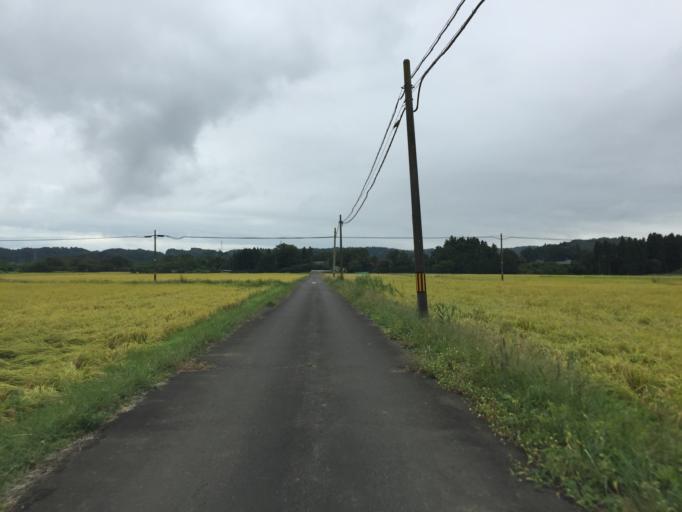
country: JP
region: Fukushima
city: Nihommatsu
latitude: 37.6588
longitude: 140.4475
